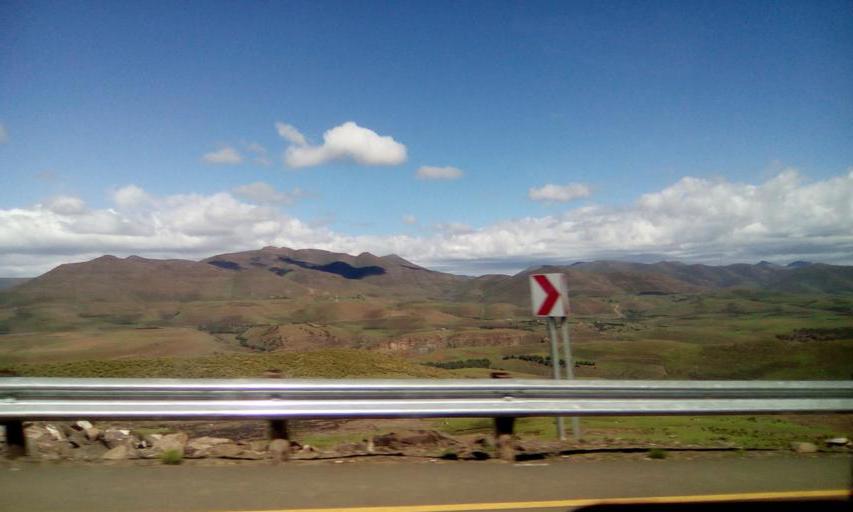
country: LS
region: Maseru
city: Nako
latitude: -29.8744
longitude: 28.0719
